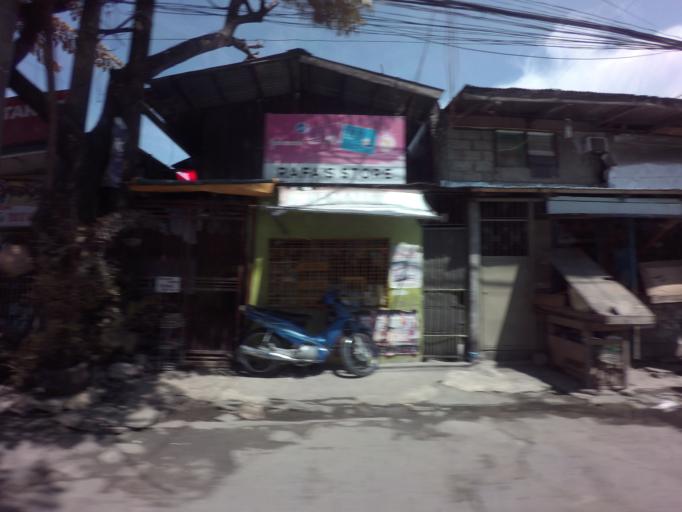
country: PH
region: Calabarzon
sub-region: Province of Rizal
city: Las Pinas
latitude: 14.4660
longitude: 120.9732
